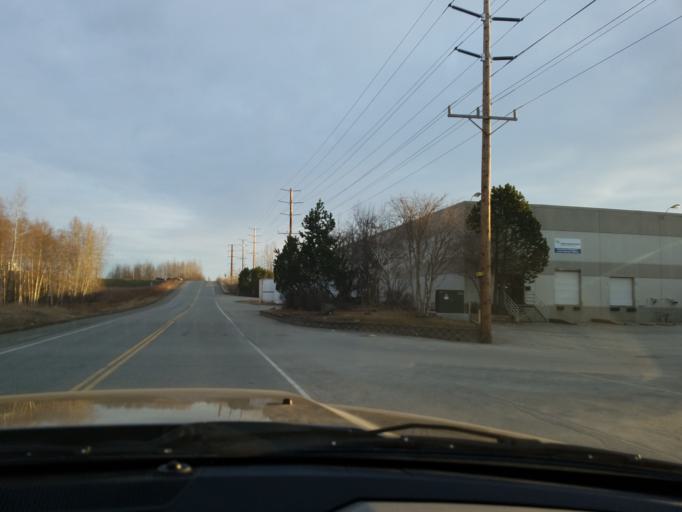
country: US
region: Alaska
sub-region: Anchorage Municipality
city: Anchorage
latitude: 61.1704
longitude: -149.9129
